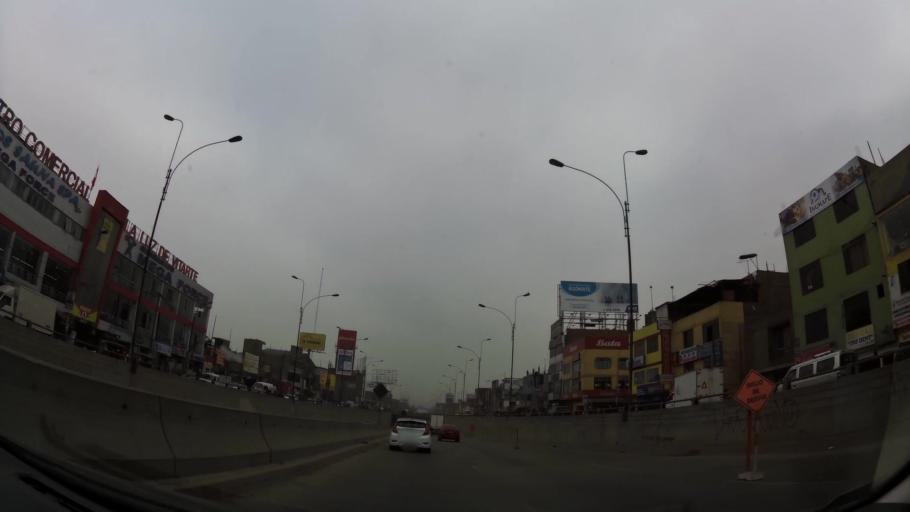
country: PE
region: Lima
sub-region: Lima
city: Vitarte
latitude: -12.0305
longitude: -76.9254
